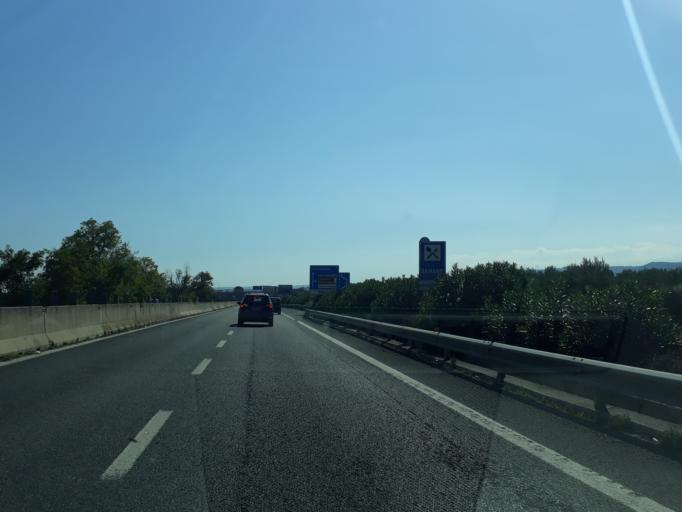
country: IT
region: Apulia
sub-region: Provincia di Bari
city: Monopoli
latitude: 40.8989
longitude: 17.3285
